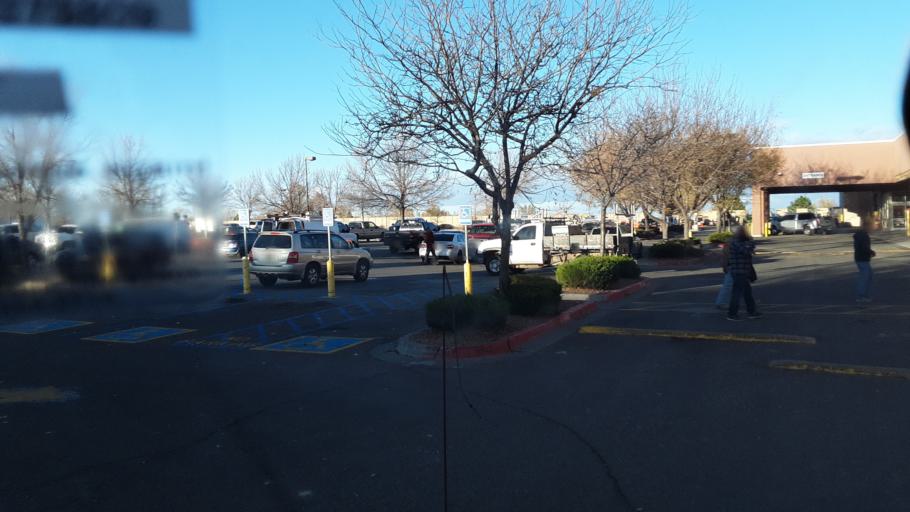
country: US
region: New Mexico
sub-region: Santa Fe County
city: Agua Fria
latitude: 35.6520
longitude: -106.0025
